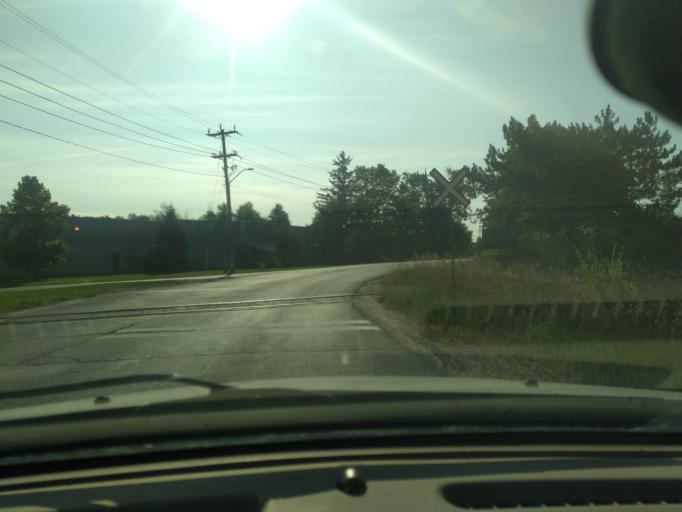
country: CA
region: Ontario
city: Barrie
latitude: 44.3569
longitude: -79.6685
